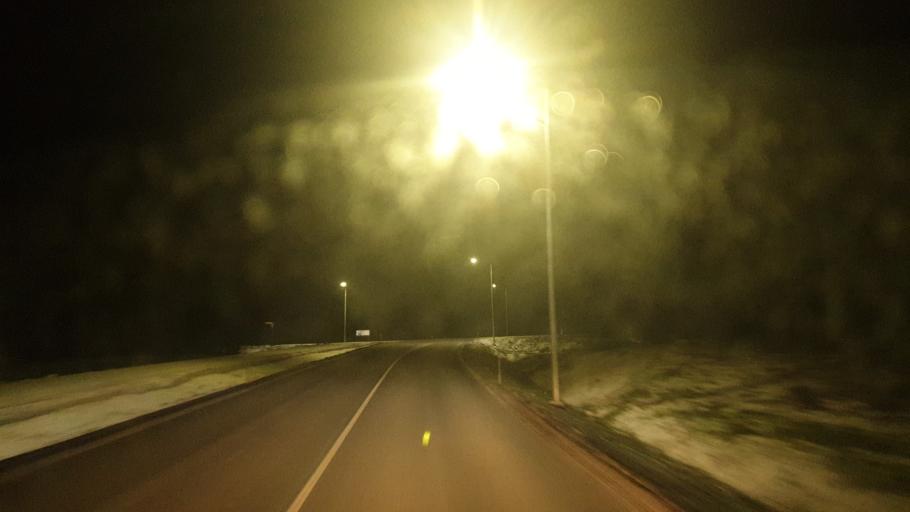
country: FI
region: Southern Savonia
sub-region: Pieksaemaeki
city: Juva
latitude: 61.8763
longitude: 27.7716
